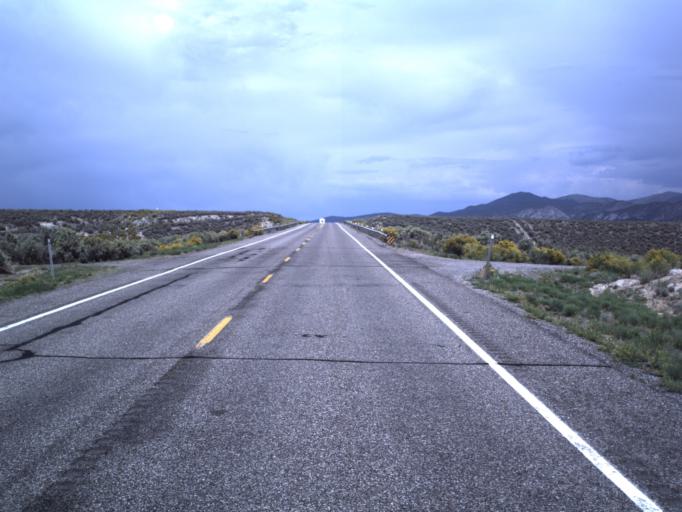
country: US
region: Utah
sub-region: Garfield County
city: Panguitch
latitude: 37.9766
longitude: -112.4043
